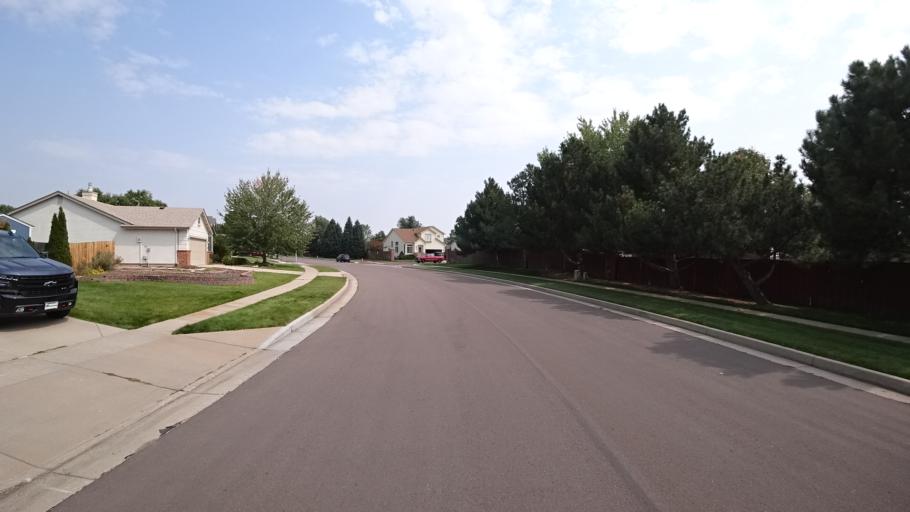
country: US
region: Colorado
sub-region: El Paso County
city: Cimarron Hills
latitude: 38.8218
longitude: -104.7393
